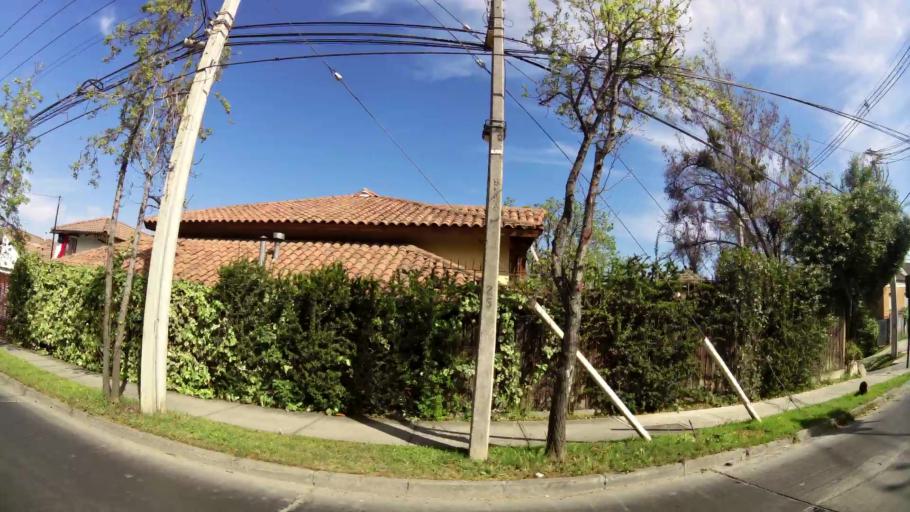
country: CL
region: Santiago Metropolitan
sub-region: Provincia de Santiago
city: Villa Presidente Frei, Nunoa, Santiago, Chile
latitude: -33.4358
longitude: -70.5372
